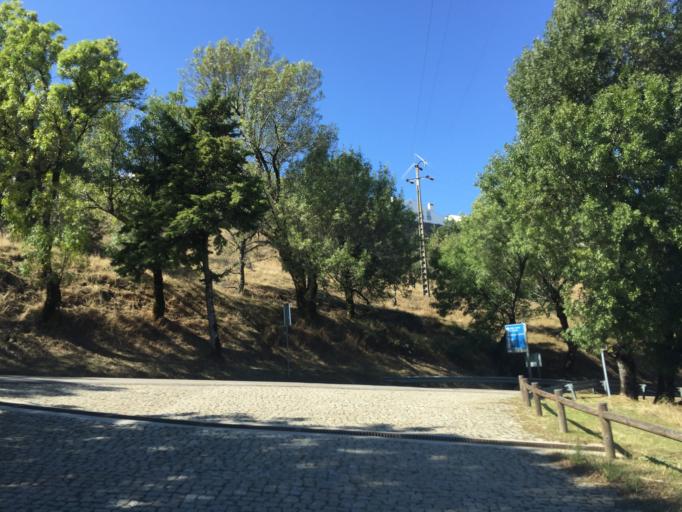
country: PT
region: Portalegre
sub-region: Marvao
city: Marvao
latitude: 39.3943
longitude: -7.3740
